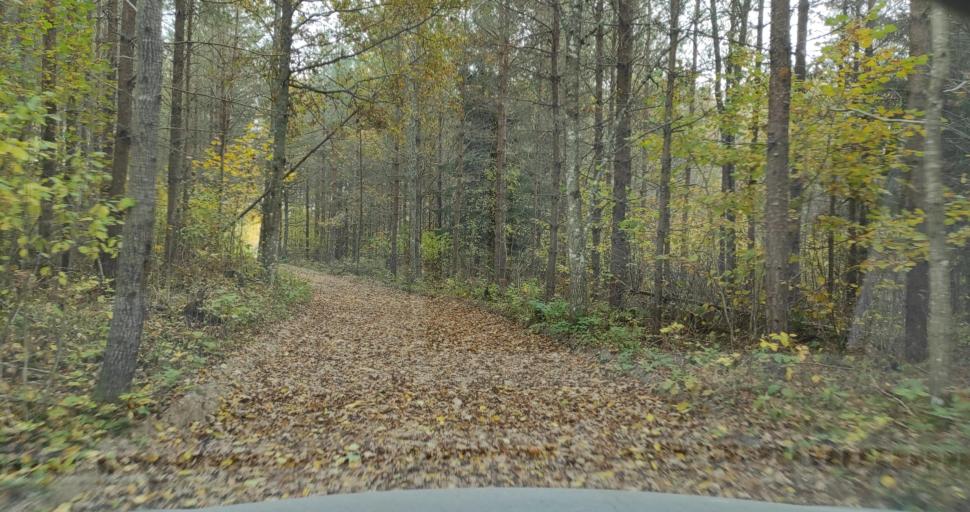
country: LV
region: Alsunga
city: Alsunga
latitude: 57.0387
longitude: 21.6991
